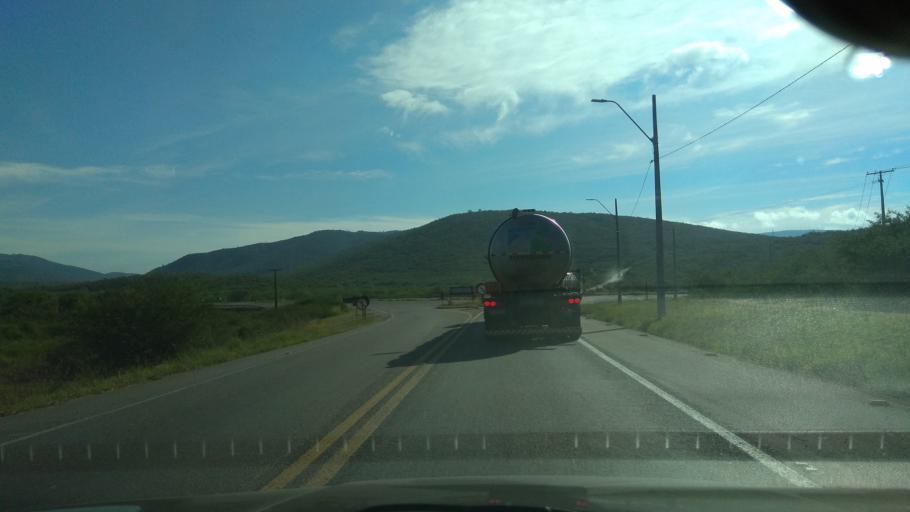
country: BR
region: Bahia
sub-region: Jequie
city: Jequie
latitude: -13.8365
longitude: -40.1067
